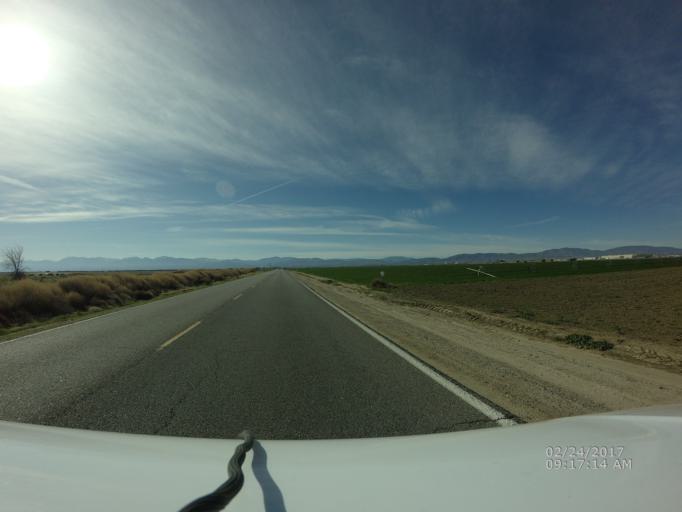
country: US
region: California
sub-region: Los Angeles County
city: Lancaster
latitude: 34.6543
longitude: -118.0410
